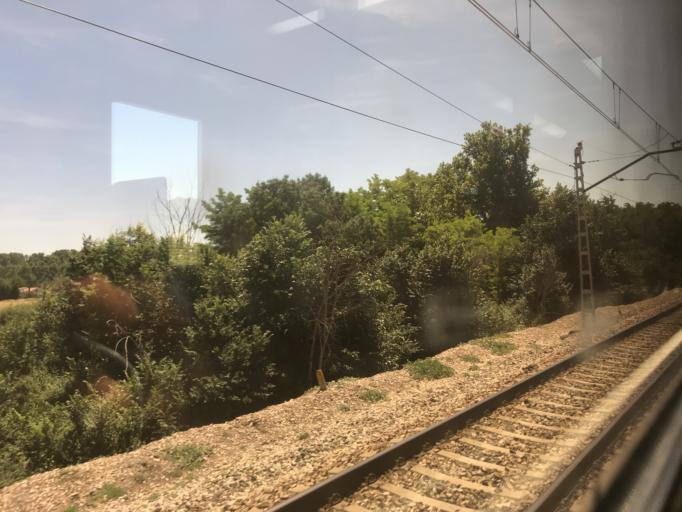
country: ES
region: Madrid
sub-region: Provincia de Madrid
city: Aranjuez
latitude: 40.0448
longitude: -3.6215
